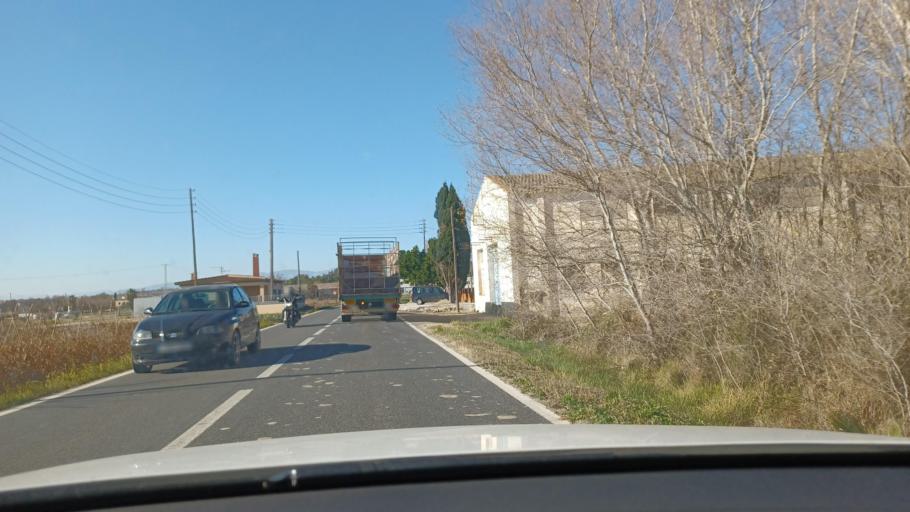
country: ES
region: Catalonia
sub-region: Provincia de Tarragona
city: Amposta
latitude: 40.7060
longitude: 0.5963
